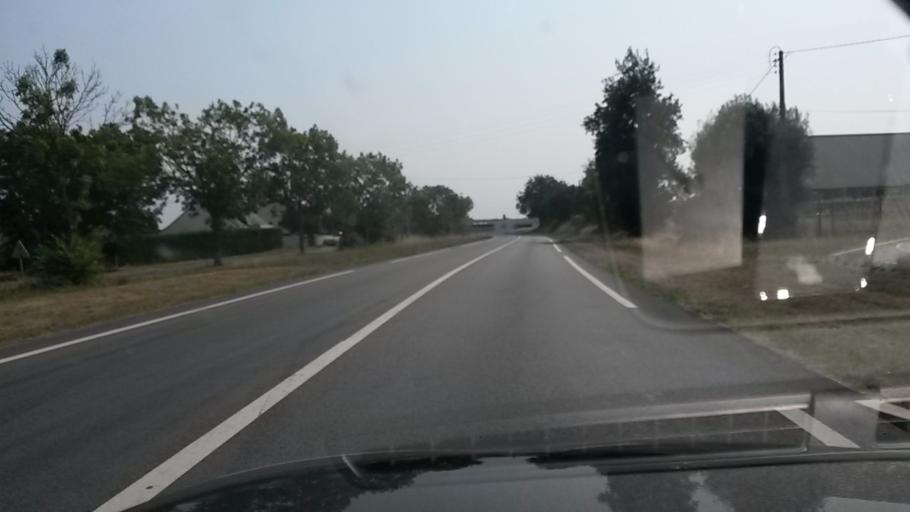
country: FR
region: Pays de la Loire
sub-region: Departement de la Loire-Atlantique
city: Ancenis
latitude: 47.3826
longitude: -1.1728
